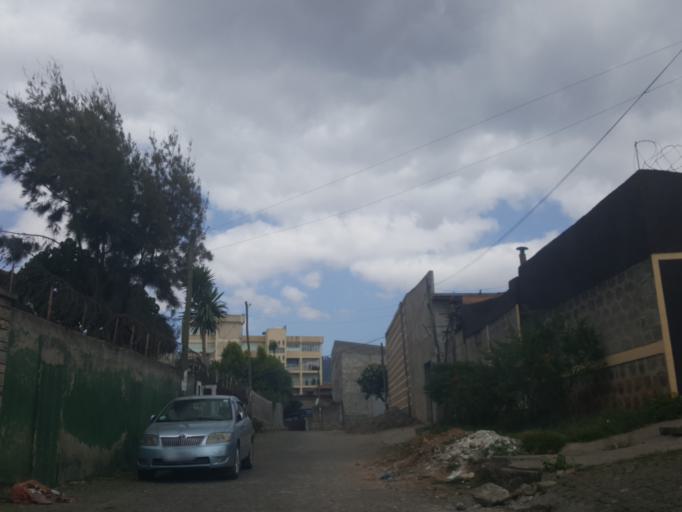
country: ET
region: Adis Abeba
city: Addis Ababa
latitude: 9.0566
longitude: 38.7180
